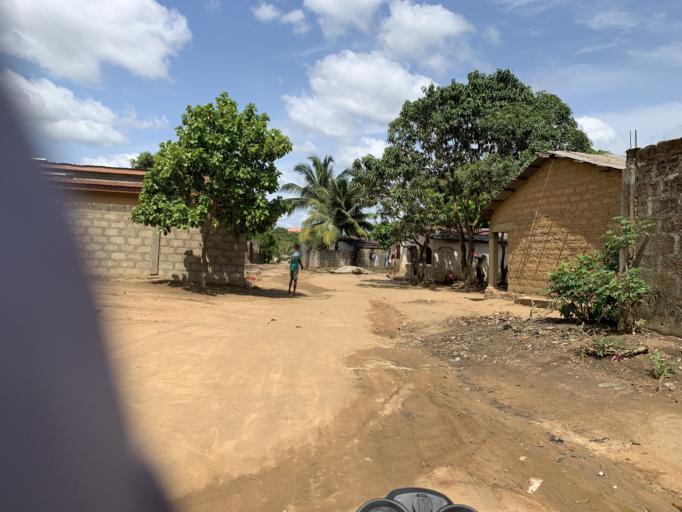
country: SL
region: Western Area
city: Waterloo
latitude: 8.3355
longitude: -13.0485
